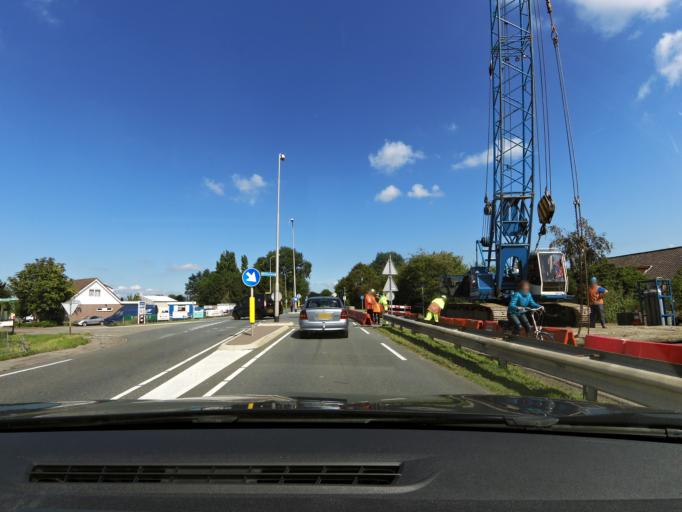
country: NL
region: North Holland
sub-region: Gemeente Uithoorn
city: Uithoorn
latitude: 52.2658
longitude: 4.8006
